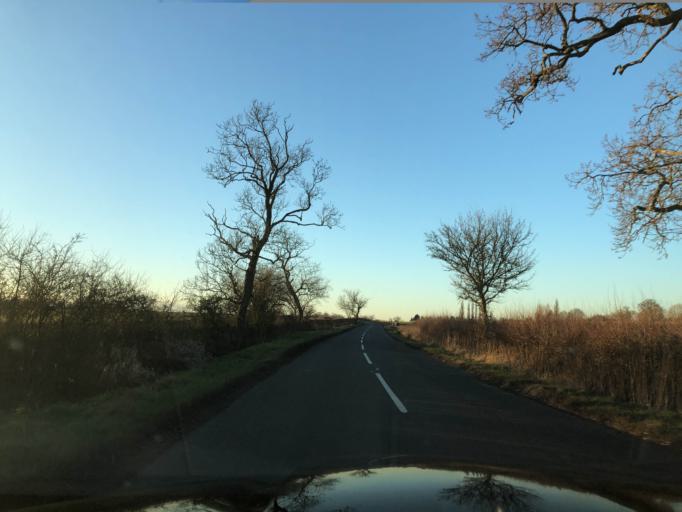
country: GB
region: England
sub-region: Warwickshire
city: Harbury
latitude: 52.2298
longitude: -1.4727
